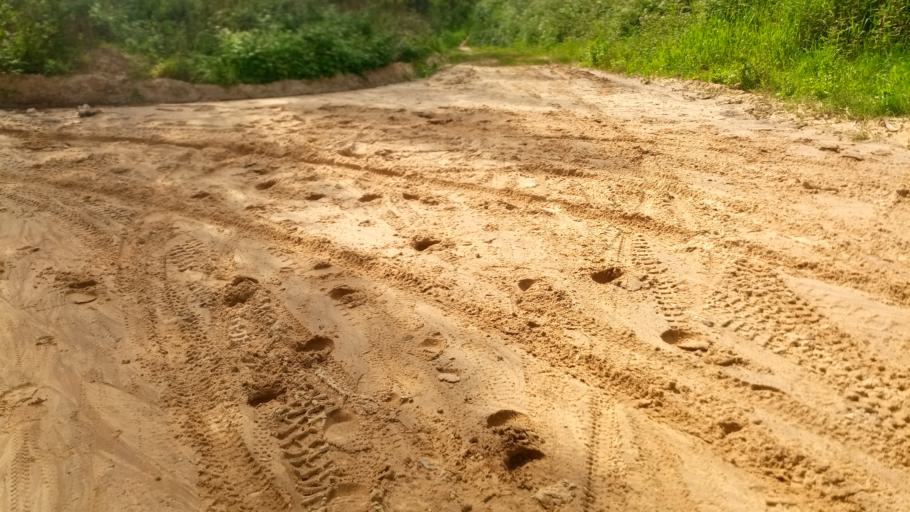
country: PT
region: Leiria
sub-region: Caldas da Rainha
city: Caldas da Rainha
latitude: 39.3997
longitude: -9.1872
